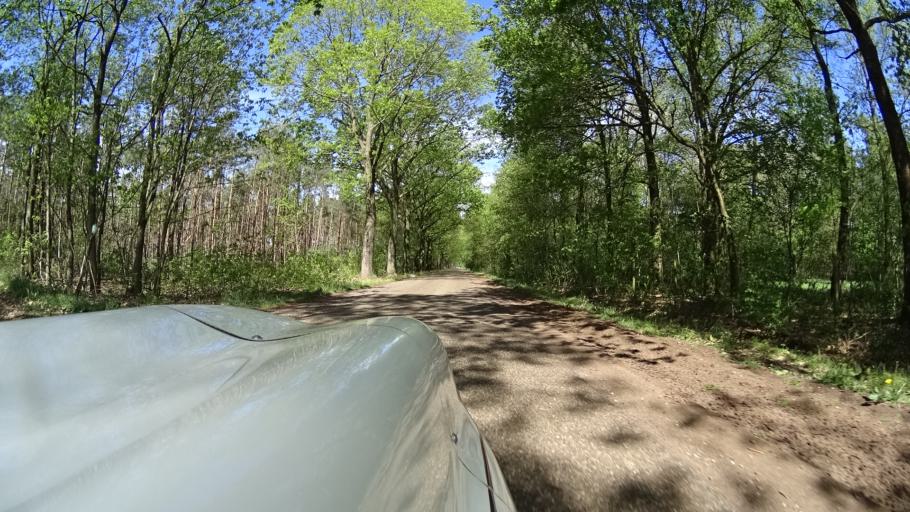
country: NL
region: North Brabant
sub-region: Gemeente Mill en Sint Hubert
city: Wilbertoord
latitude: 51.5969
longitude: 5.8097
